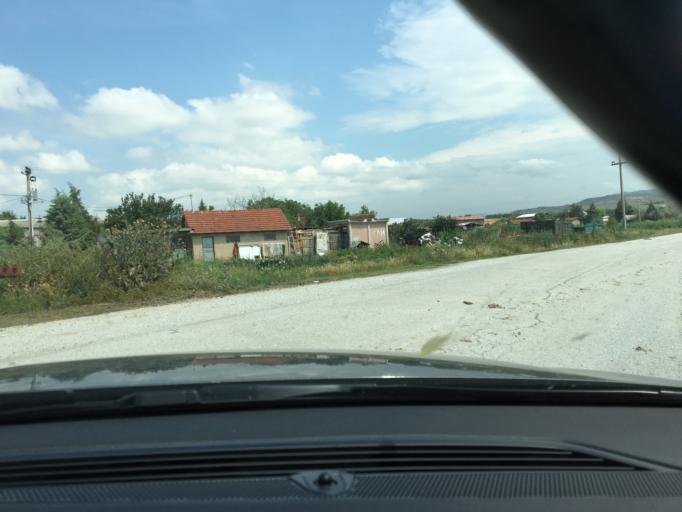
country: MK
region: Sveti Nikole
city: Sveti Nikole
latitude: 41.8796
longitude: 21.9371
